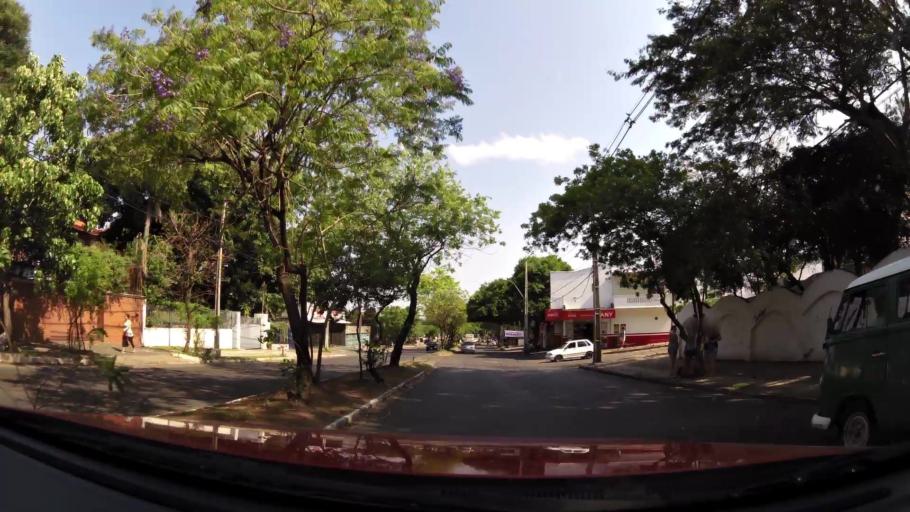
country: PY
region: Asuncion
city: Asuncion
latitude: -25.3050
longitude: -57.6321
